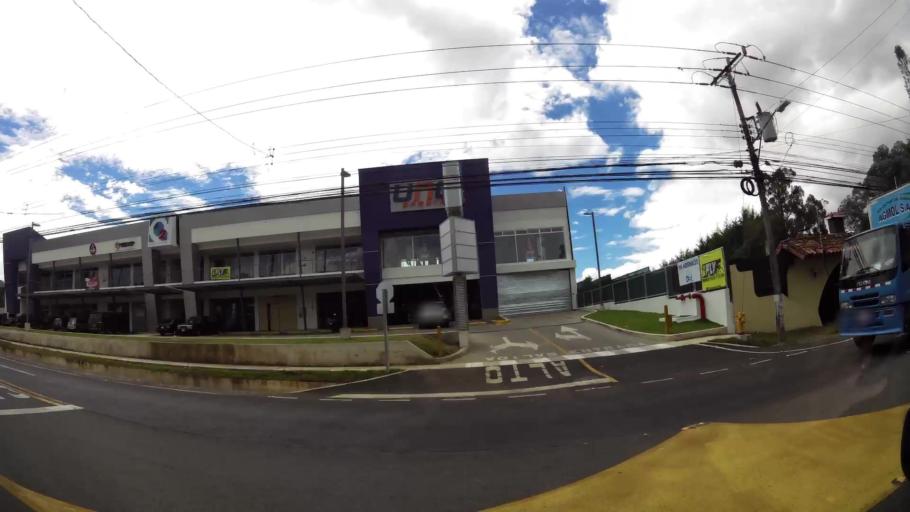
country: CR
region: Cartago
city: San Diego
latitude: 9.9107
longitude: -84.0132
